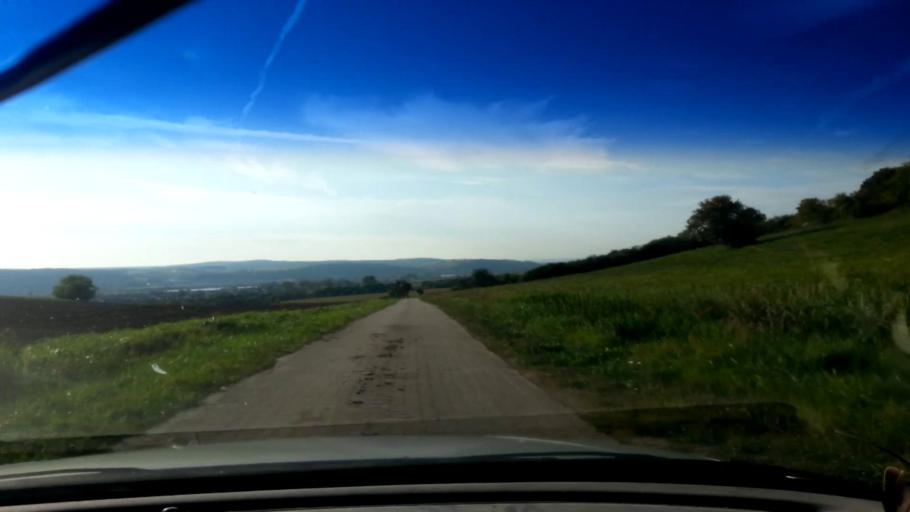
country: DE
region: Bavaria
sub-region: Upper Franconia
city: Lauter
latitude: 49.9476
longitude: 10.7671
